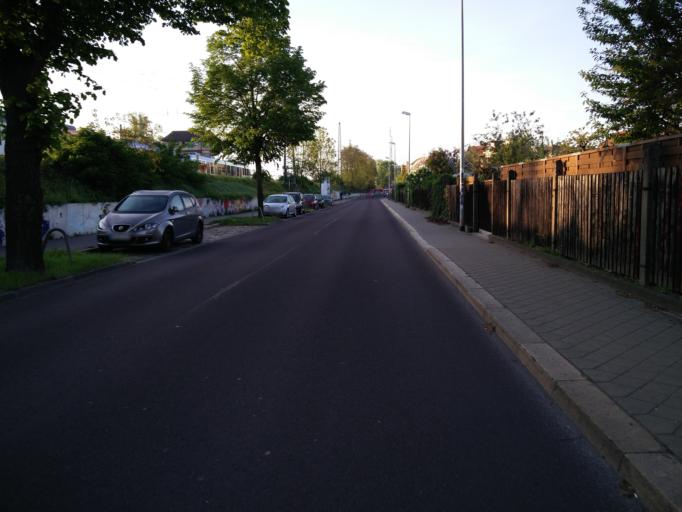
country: DE
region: Saxony-Anhalt
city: Magdeburg
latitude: 52.1121
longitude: 11.6267
